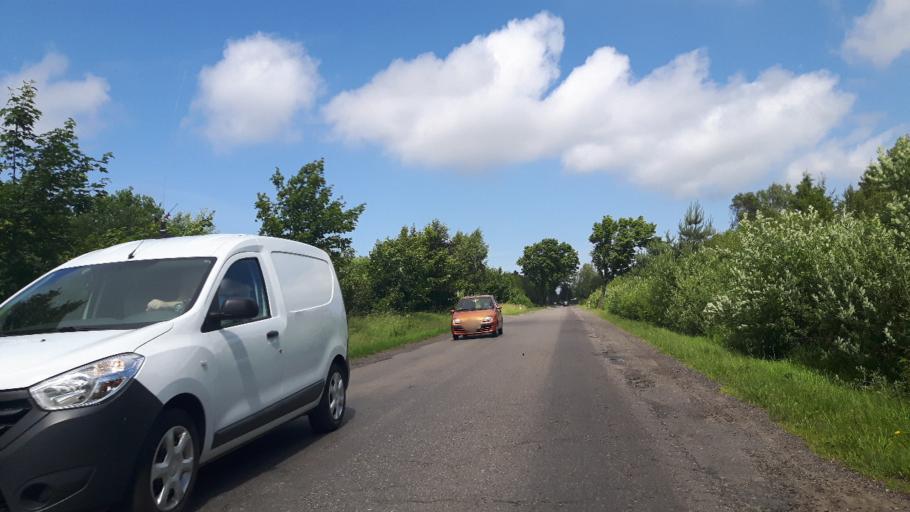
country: PL
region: Pomeranian Voivodeship
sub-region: Powiat slupski
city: Ustka
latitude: 54.5612
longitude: 16.8452
